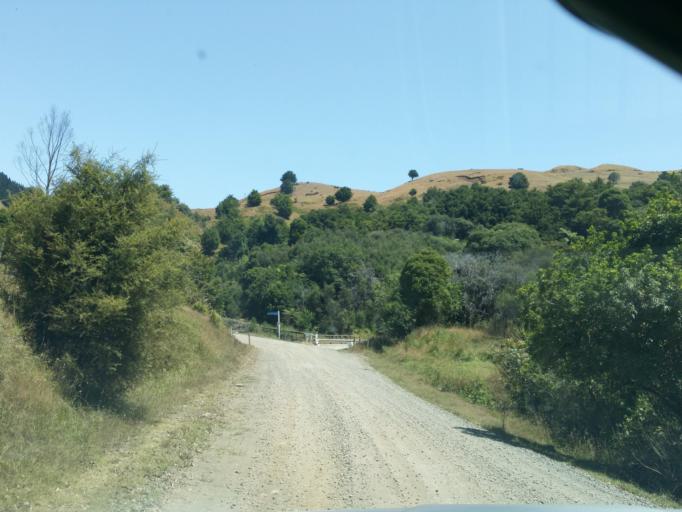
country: NZ
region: Northland
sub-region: Far North District
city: Waimate North
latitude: -35.6200
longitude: 173.7301
